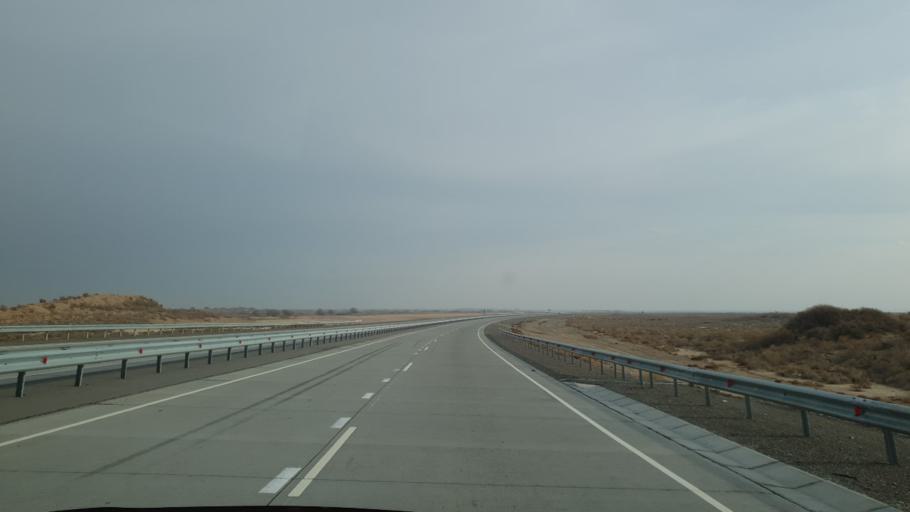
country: KZ
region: Almaty Oblysy
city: Kegen
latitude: 43.7721
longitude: 79.1559
